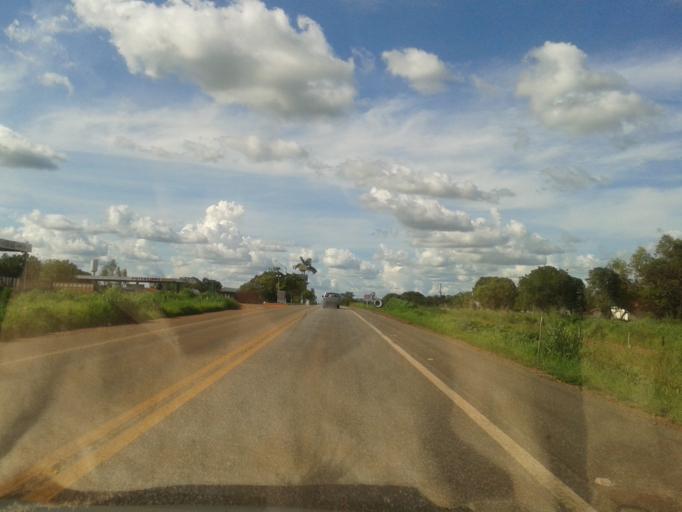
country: BR
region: Goias
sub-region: Mozarlandia
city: Mozarlandia
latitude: -14.7648
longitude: -50.5382
